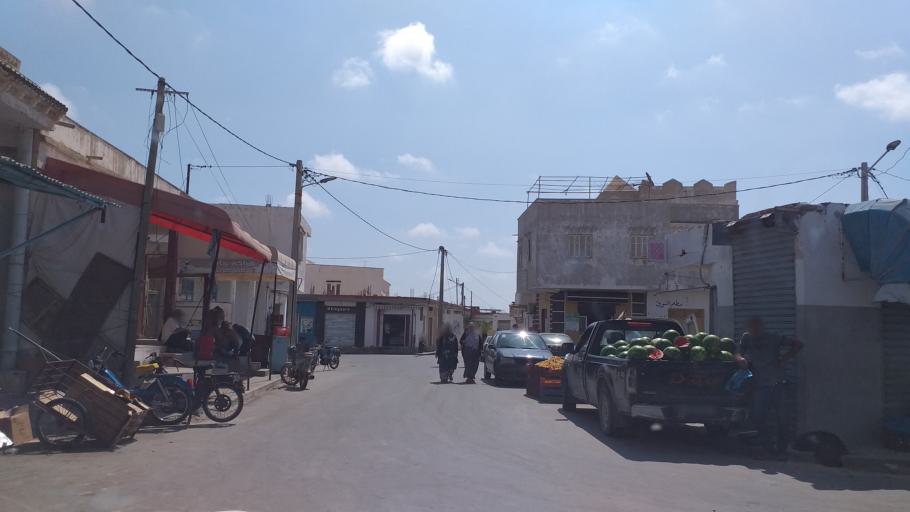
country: TN
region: Qabis
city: Gabes
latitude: 33.9399
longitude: 10.0664
